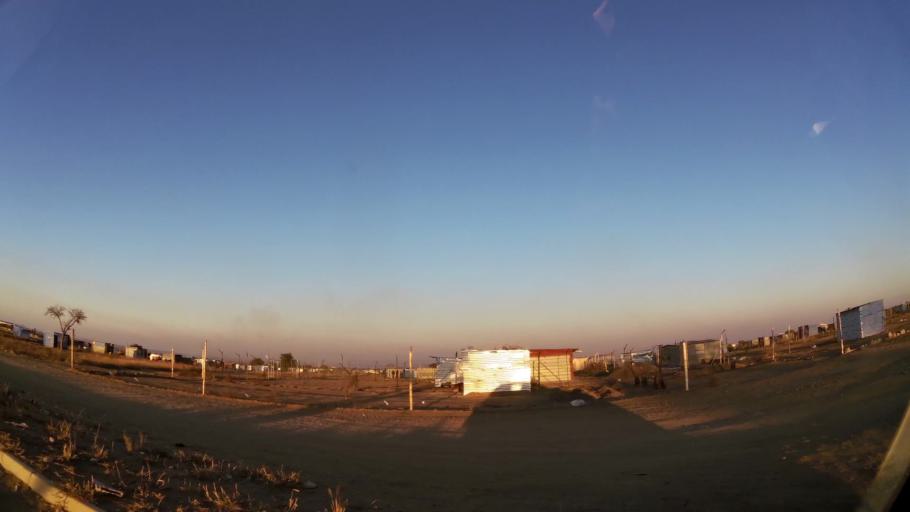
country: ZA
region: Limpopo
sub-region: Capricorn District Municipality
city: Polokwane
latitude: -23.8642
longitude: 29.3731
